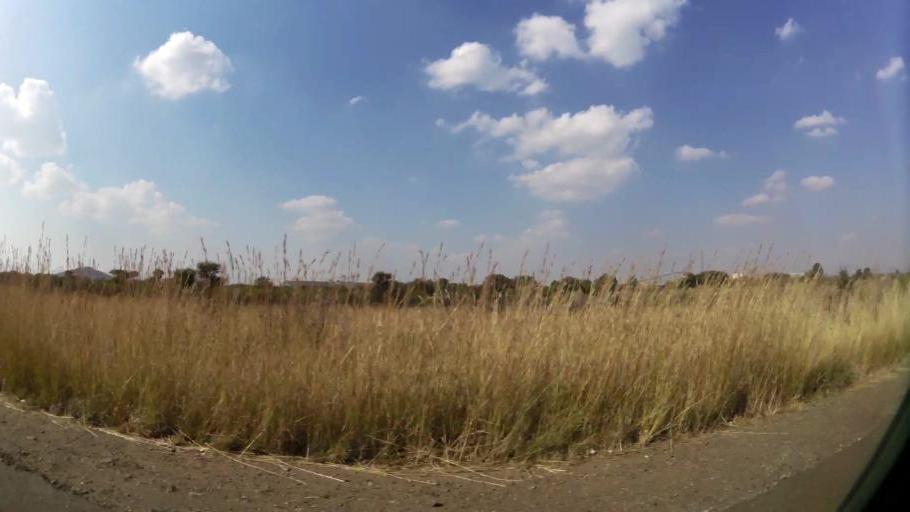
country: ZA
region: North-West
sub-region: Bojanala Platinum District Municipality
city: Mogwase
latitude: -25.4488
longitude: 27.0880
